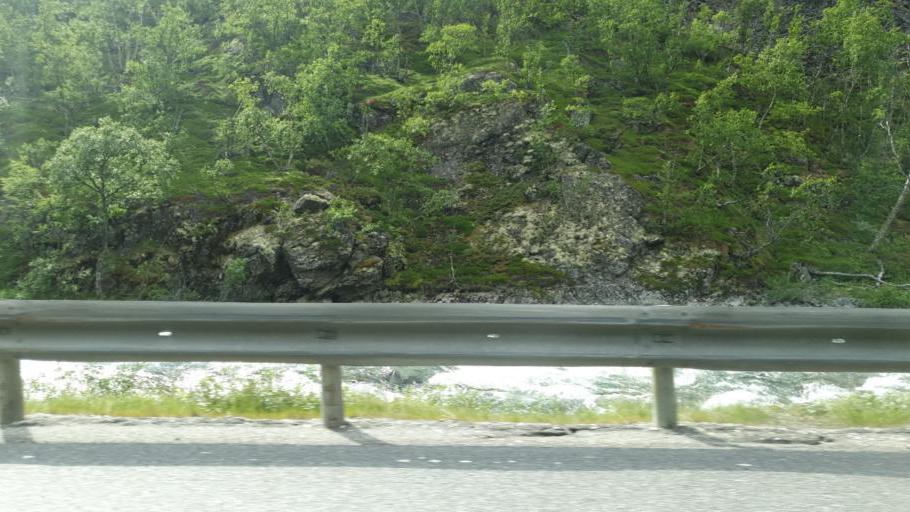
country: NO
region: Sor-Trondelag
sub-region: Oppdal
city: Oppdal
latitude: 62.3513
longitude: 9.6321
